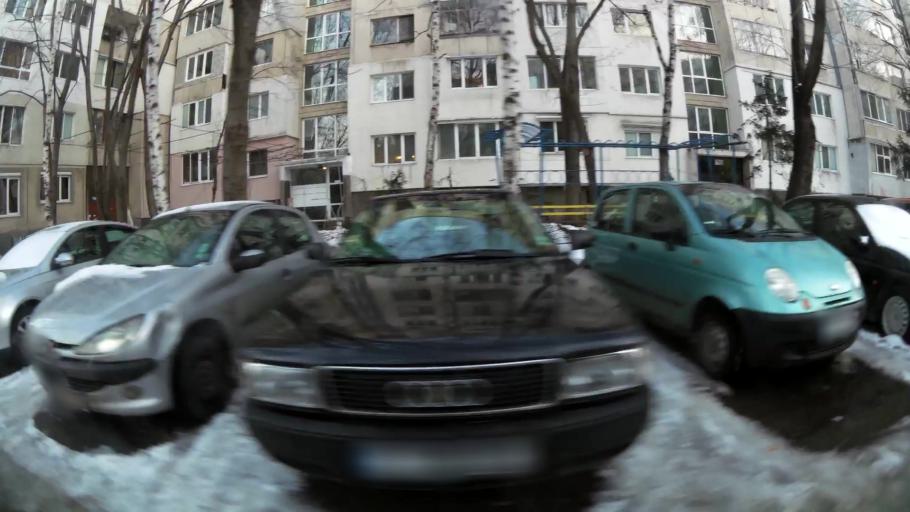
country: BG
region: Sofia-Capital
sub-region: Stolichna Obshtina
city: Sofia
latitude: 42.6843
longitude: 23.3730
